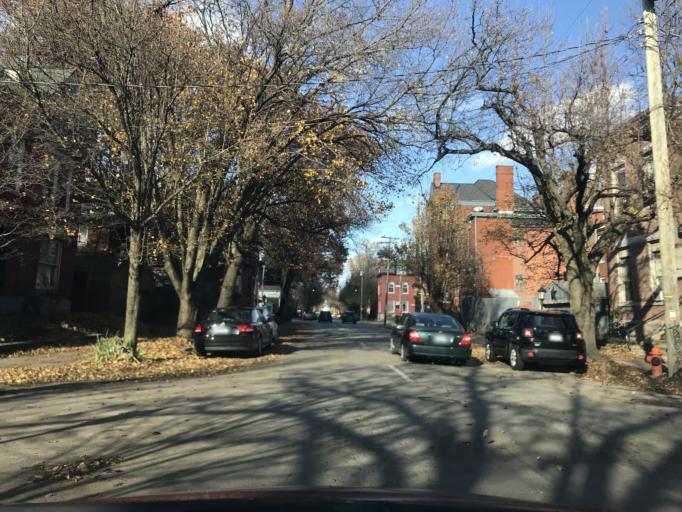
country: US
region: Kentucky
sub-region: Jefferson County
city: Louisville
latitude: 38.2318
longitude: -85.7575
